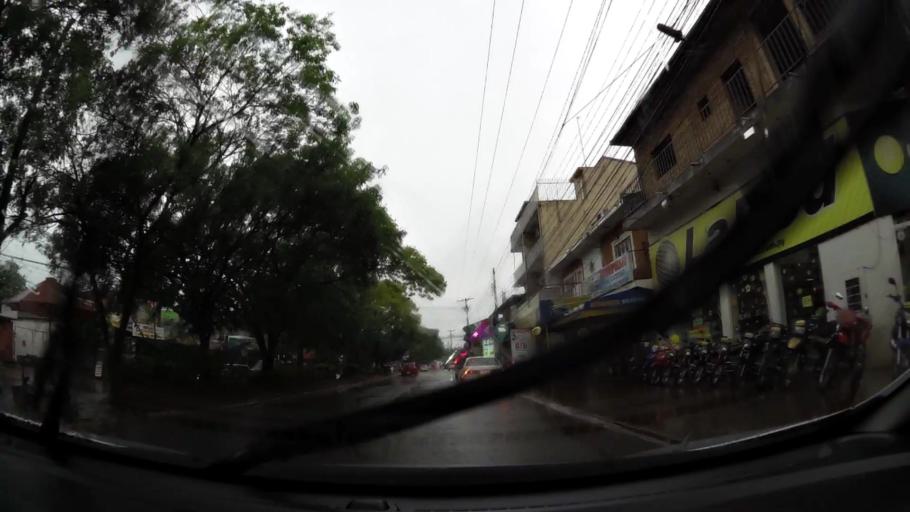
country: PY
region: Alto Parana
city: Ciudad del Este
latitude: -25.5061
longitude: -54.6696
